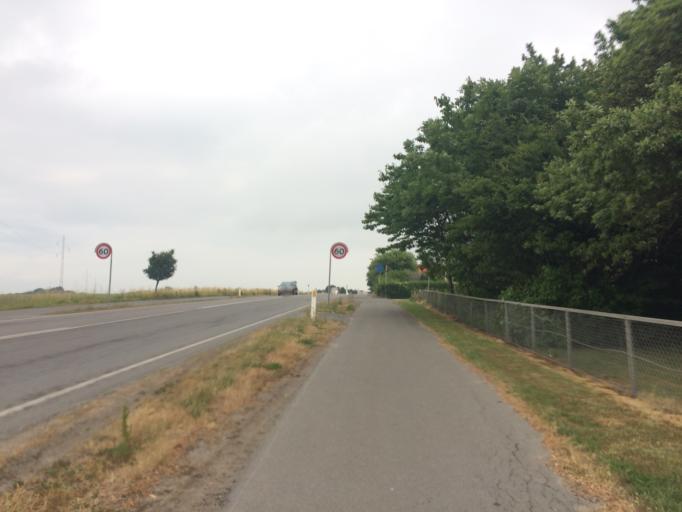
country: DK
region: Capital Region
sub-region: Bornholm Kommune
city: Ronne
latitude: 55.1064
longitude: 14.7385
